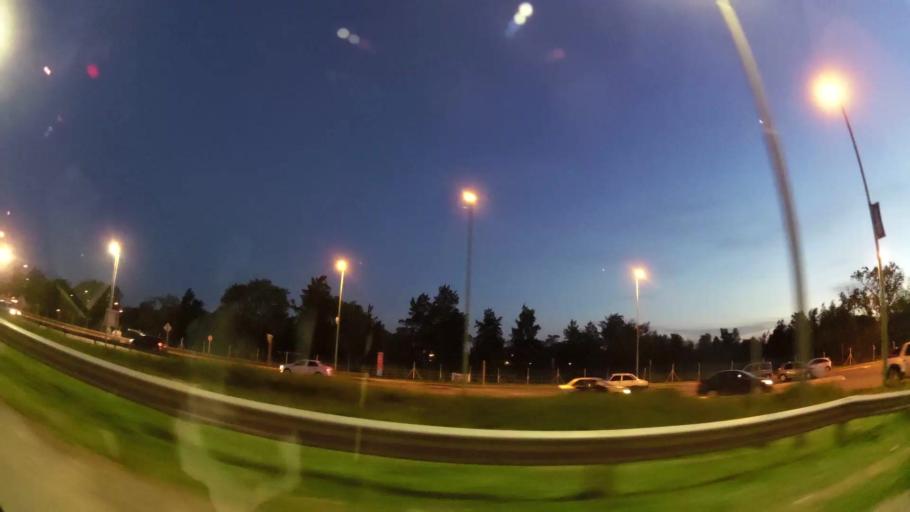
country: AR
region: Buenos Aires
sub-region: Partido de Quilmes
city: Quilmes
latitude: -34.7535
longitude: -58.1934
